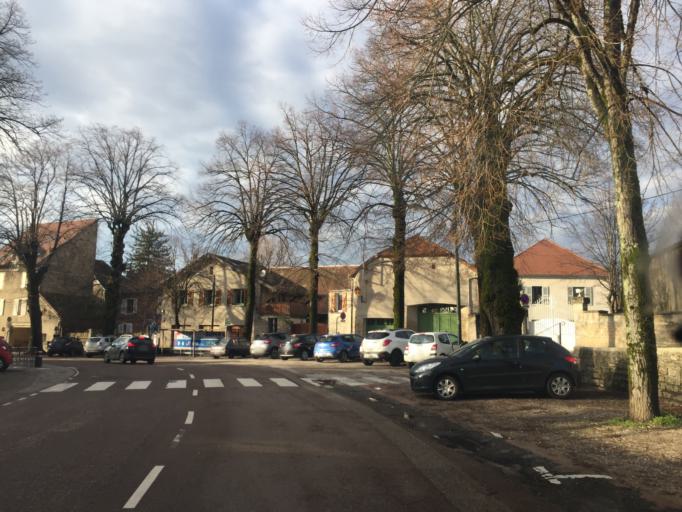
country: FR
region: Franche-Comte
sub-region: Departement du Jura
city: Arbois
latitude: 46.9045
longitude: 5.7727
